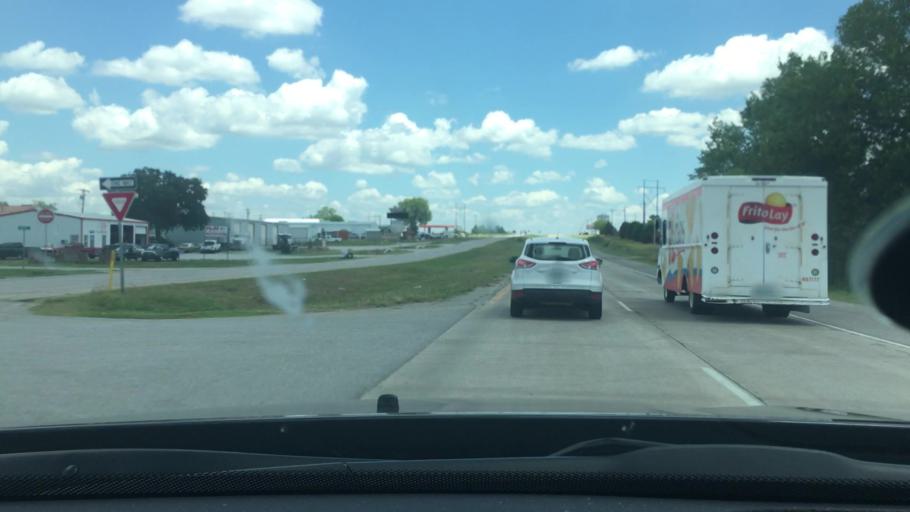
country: US
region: Oklahoma
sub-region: Carter County
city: Lone Grove
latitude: 34.1728
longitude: -97.2263
